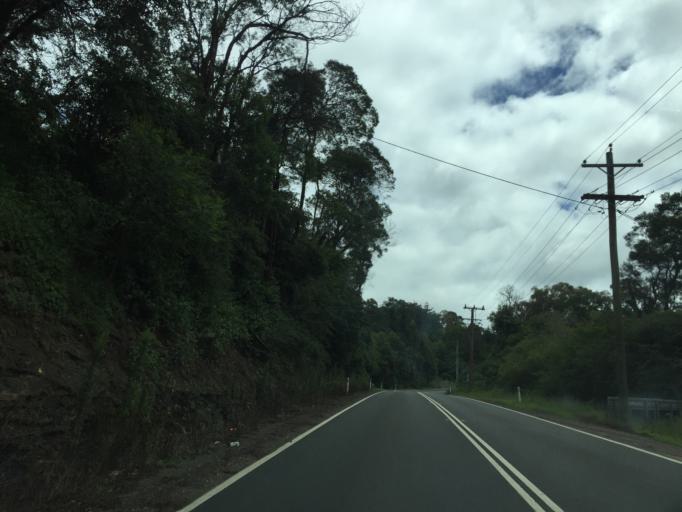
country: AU
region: New South Wales
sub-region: Hawkesbury
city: Richmond
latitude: -33.5284
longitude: 150.6295
